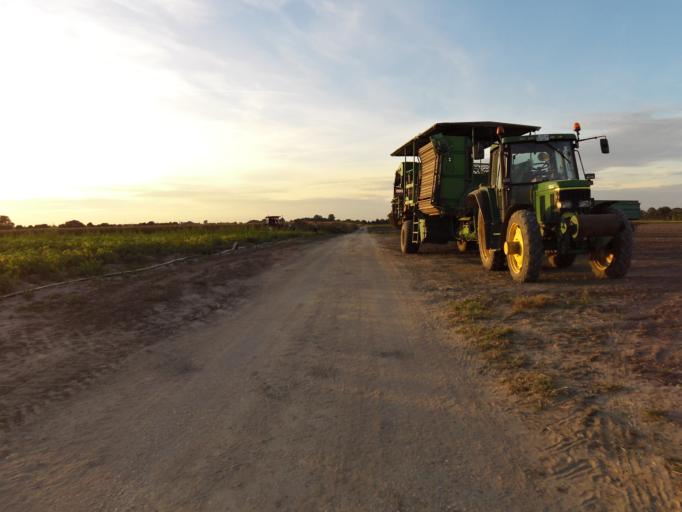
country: DE
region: Rheinland-Pfalz
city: Beindersheim
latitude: 49.5717
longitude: 8.3347
